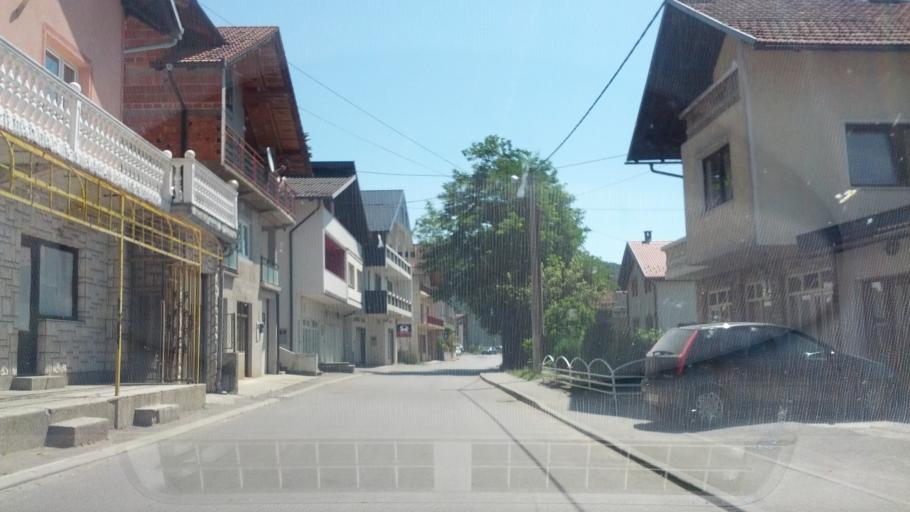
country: BA
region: Federation of Bosnia and Herzegovina
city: Bosanska Krupa
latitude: 44.8871
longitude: 16.1491
